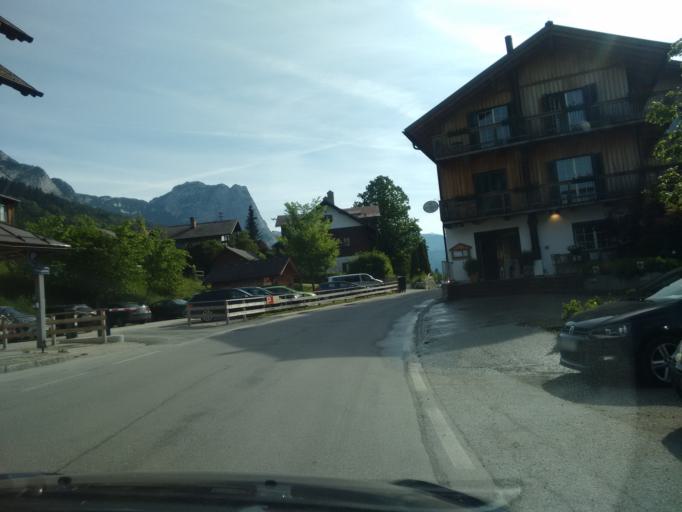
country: AT
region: Styria
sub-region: Politischer Bezirk Liezen
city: Bad Aussee
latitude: 47.6234
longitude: 13.8300
